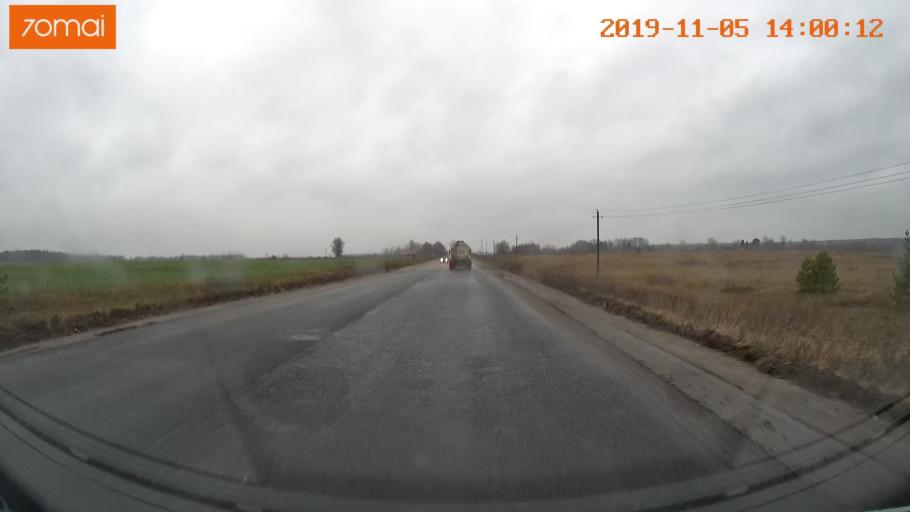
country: RU
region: Ivanovo
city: Kitovo
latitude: 57.0151
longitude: 41.2538
